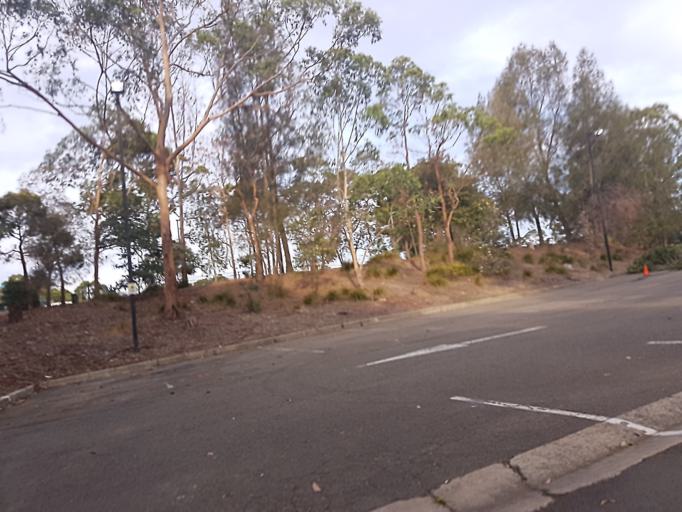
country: AU
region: New South Wales
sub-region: North Sydney
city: St Leonards
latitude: -33.8125
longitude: 151.2017
